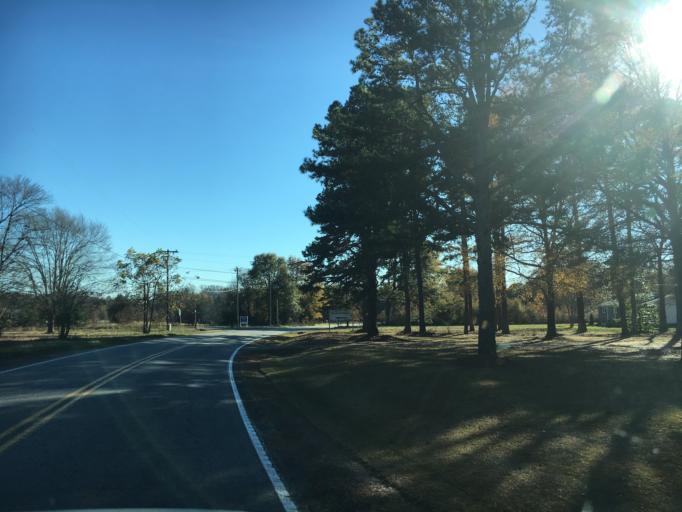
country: US
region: South Carolina
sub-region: Spartanburg County
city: Duncan
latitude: 35.0054
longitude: -82.1758
